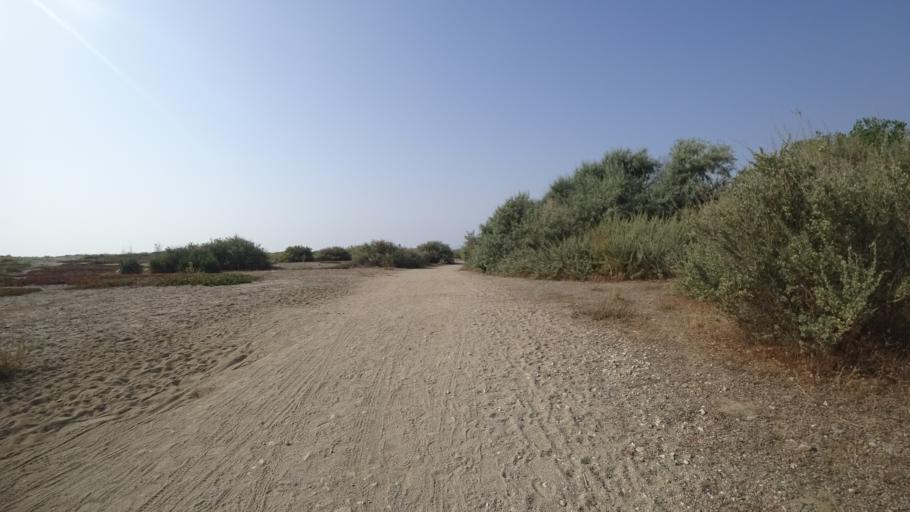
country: FR
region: Languedoc-Roussillon
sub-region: Departement des Pyrenees-Orientales
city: Sainte-Marie-Plage
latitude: 42.7411
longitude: 3.0367
